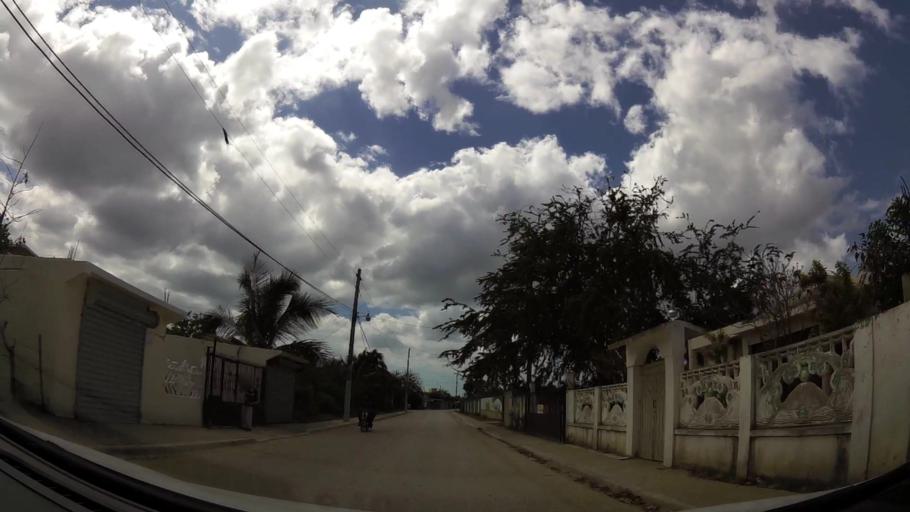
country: DO
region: Santo Domingo
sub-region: Santo Domingo
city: Boca Chica
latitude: 18.4525
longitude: -69.6351
